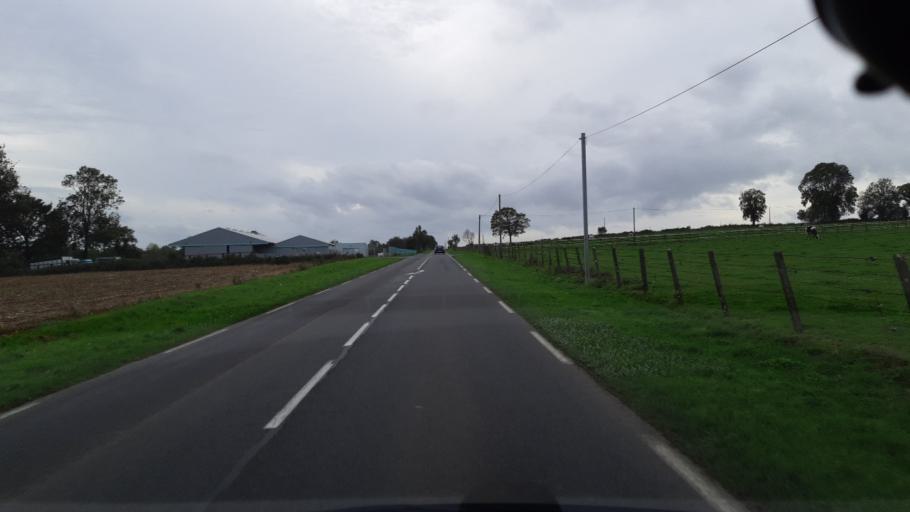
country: FR
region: Lower Normandy
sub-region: Departement de la Manche
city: Gavray
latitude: 48.9374
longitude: -1.3528
